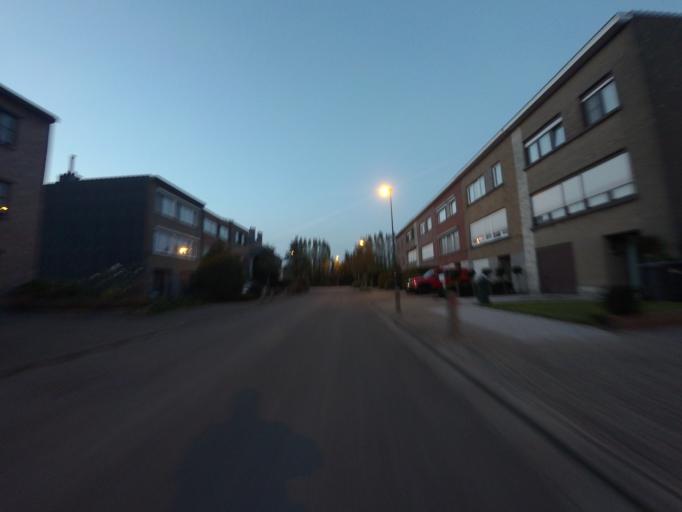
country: BE
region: Flanders
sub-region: Provincie Vlaams-Brabant
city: Zaventem
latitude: 50.8854
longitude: 4.4810
